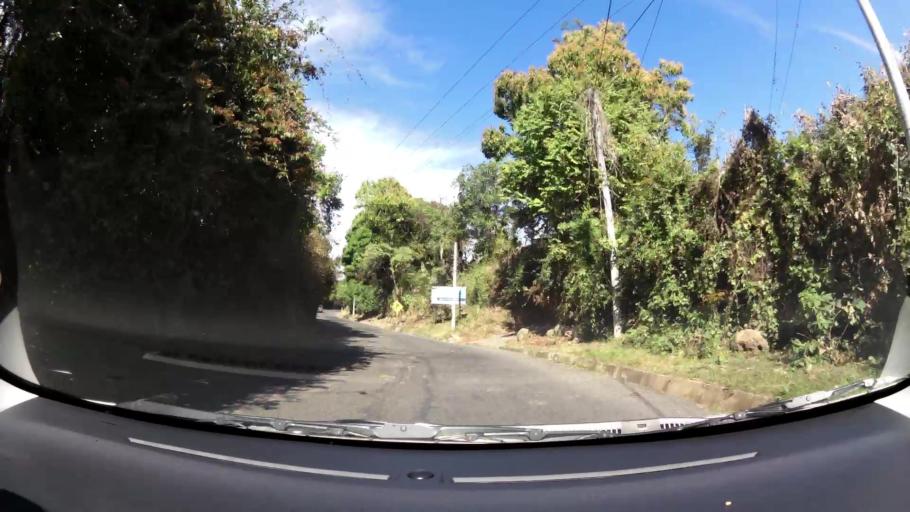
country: SV
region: Cuscatlan
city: Suchitoto
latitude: 13.9298
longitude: -89.0321
